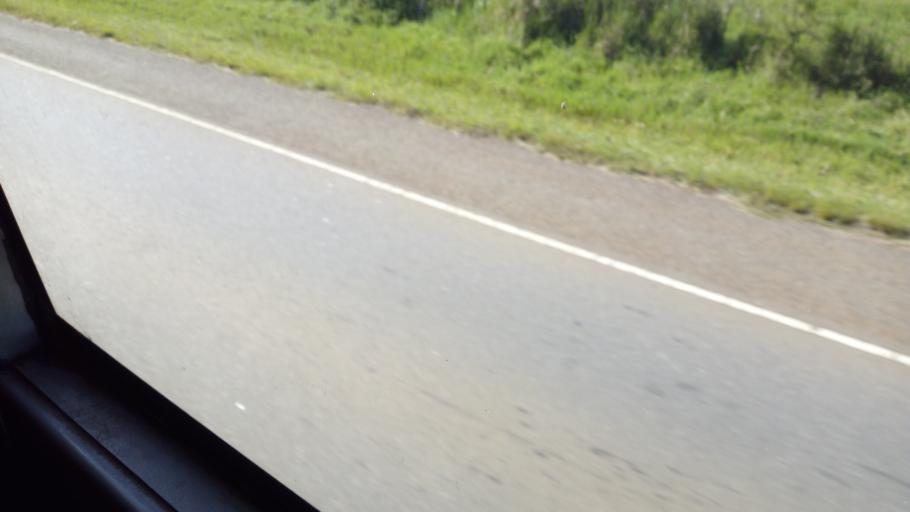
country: UG
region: Central Region
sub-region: Lyantonde District
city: Lyantonde
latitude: -0.4327
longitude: 31.0958
